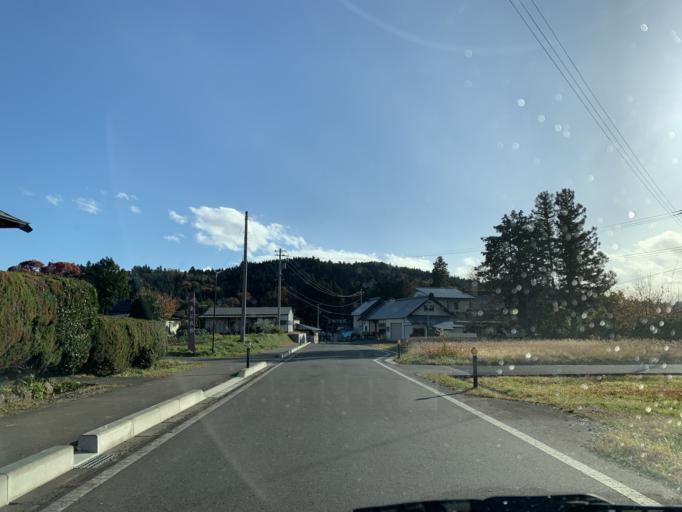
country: JP
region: Iwate
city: Ichinoseki
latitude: 39.0096
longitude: 141.0968
